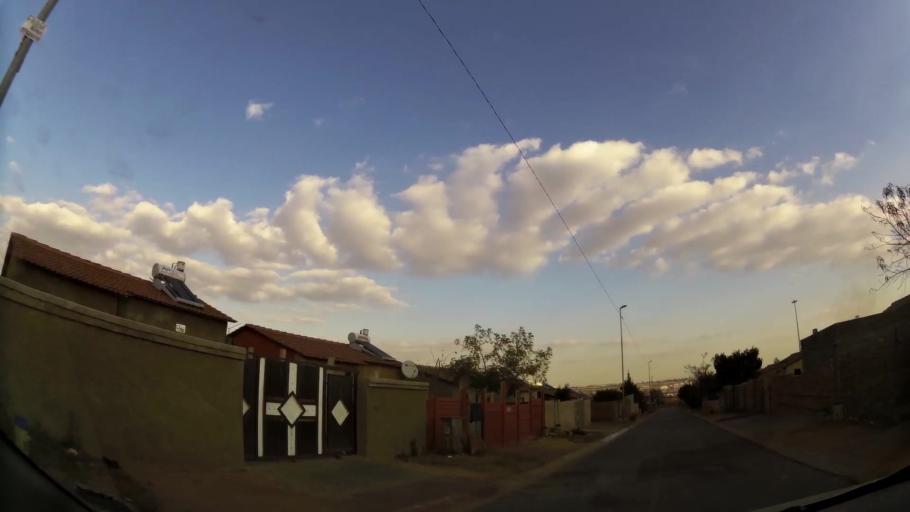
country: ZA
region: Gauteng
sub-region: West Rand District Municipality
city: Krugersdorp
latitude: -26.0770
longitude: 27.7600
